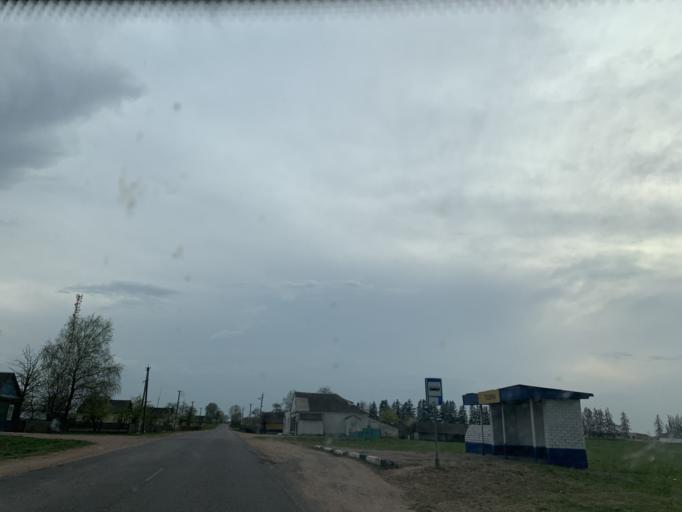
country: BY
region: Minsk
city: Kapyl'
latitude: 53.2798
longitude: 26.9760
